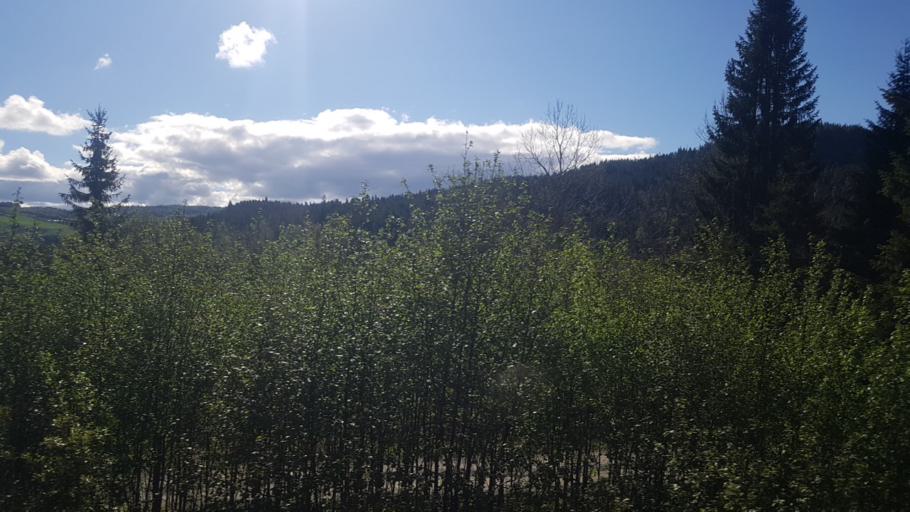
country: NO
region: Sor-Trondelag
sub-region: Midtre Gauldal
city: Storen
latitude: 62.9424
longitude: 10.1860
